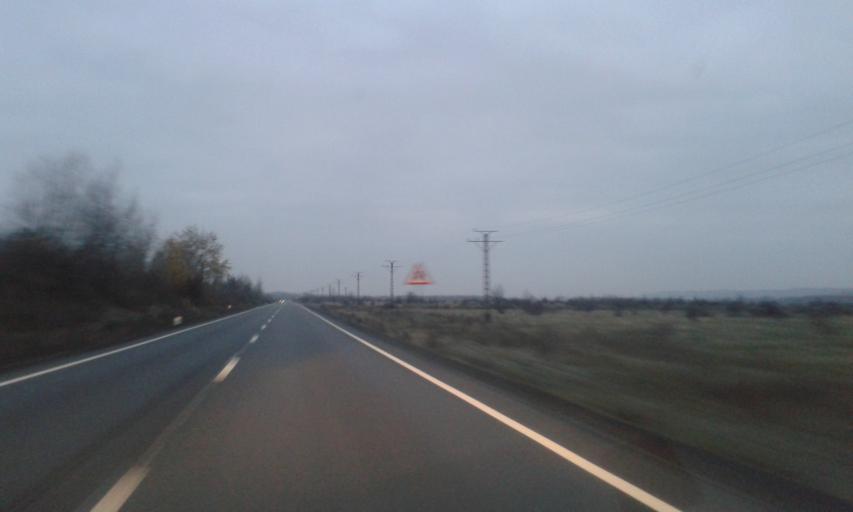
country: RO
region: Gorj
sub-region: Comuna Bumbesti-Jiu
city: Bumbesti-Jiu
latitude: 45.1503
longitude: 23.3722
